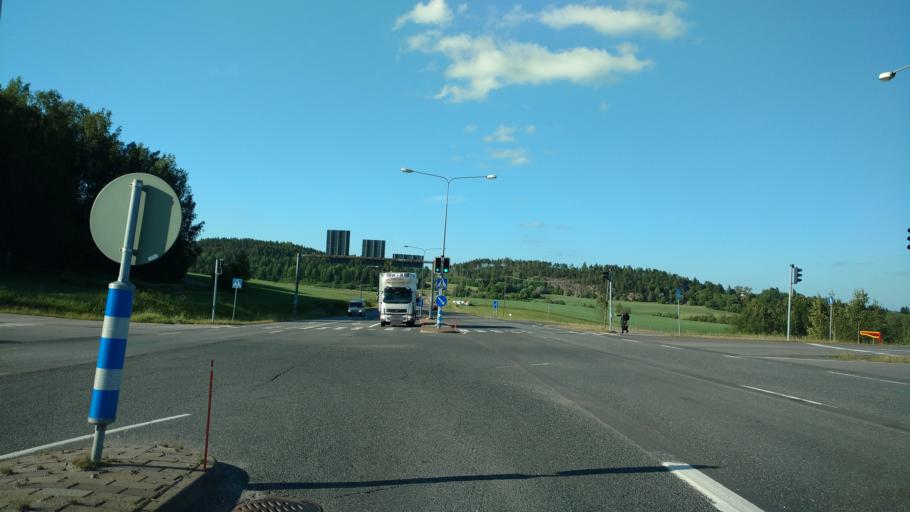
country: FI
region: Varsinais-Suomi
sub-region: Salo
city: Salo
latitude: 60.4190
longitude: 23.1664
